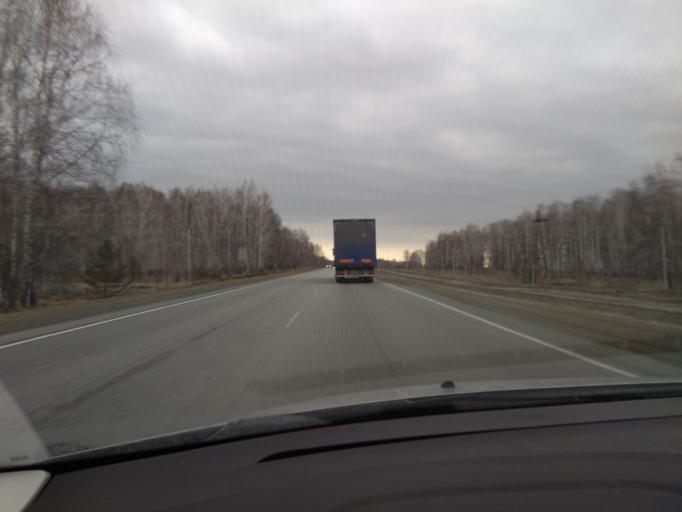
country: RU
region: Chelyabinsk
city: Tyubuk
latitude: 55.8665
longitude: 61.1569
